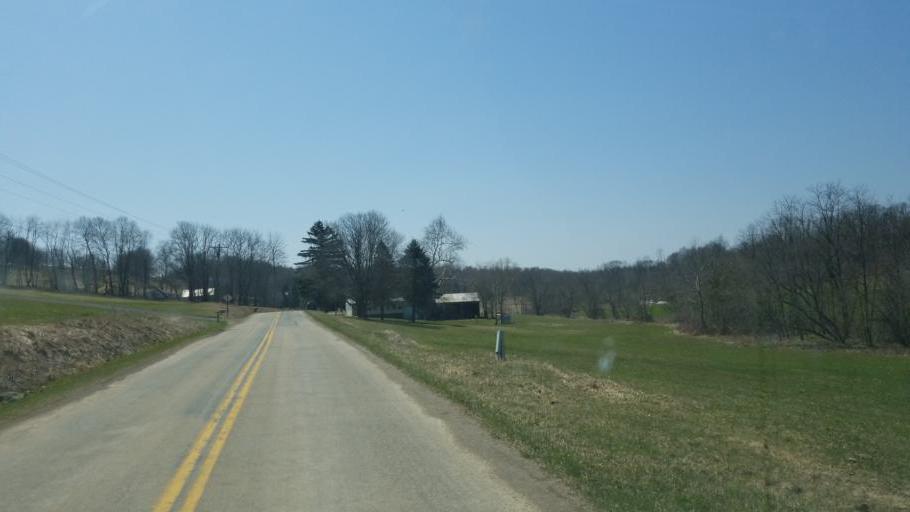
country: US
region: Ohio
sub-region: Ashland County
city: Loudonville
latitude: 40.7355
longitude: -82.2535
